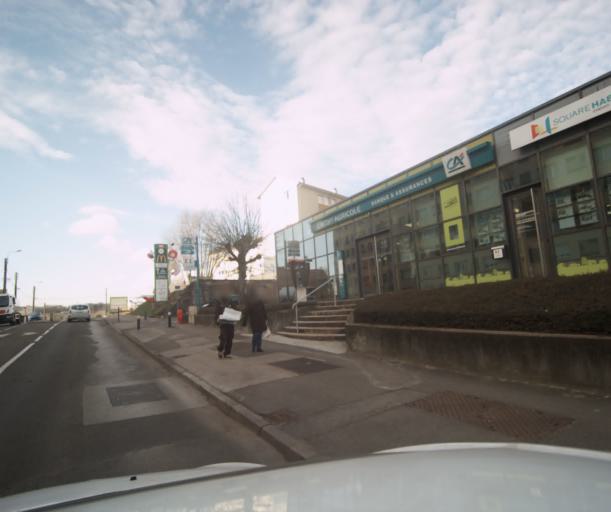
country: FR
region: Franche-Comte
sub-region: Departement du Doubs
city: Besancon
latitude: 47.2574
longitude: 6.0114
